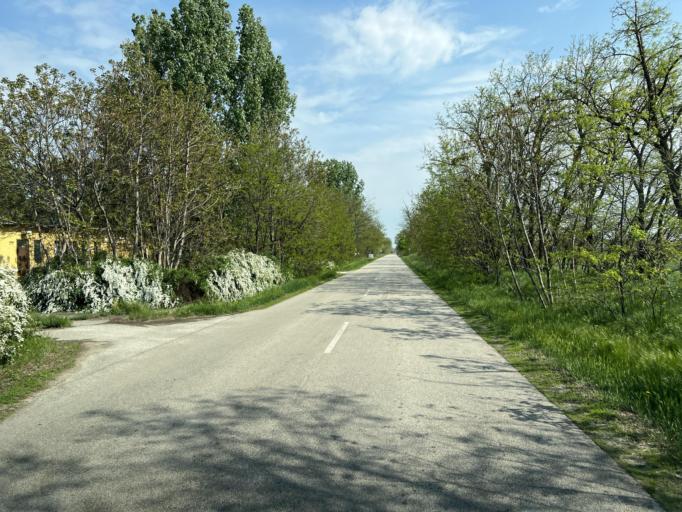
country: HU
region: Pest
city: Kocser
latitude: 47.0289
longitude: 19.9369
